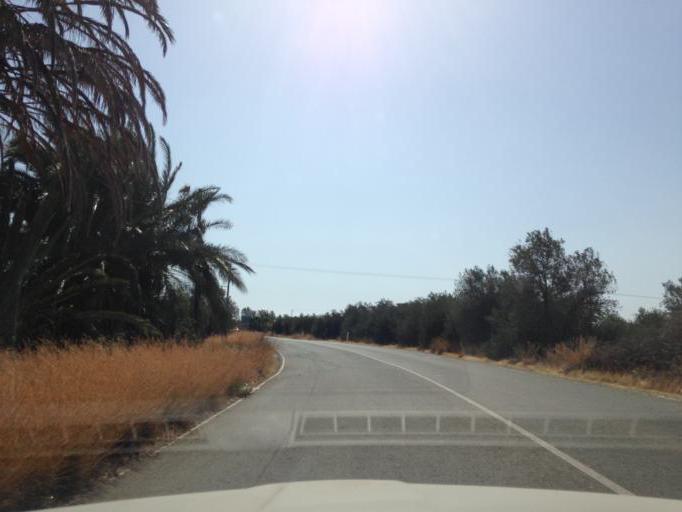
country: CY
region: Pafos
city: Mesogi
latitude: 34.7167
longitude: 32.5515
